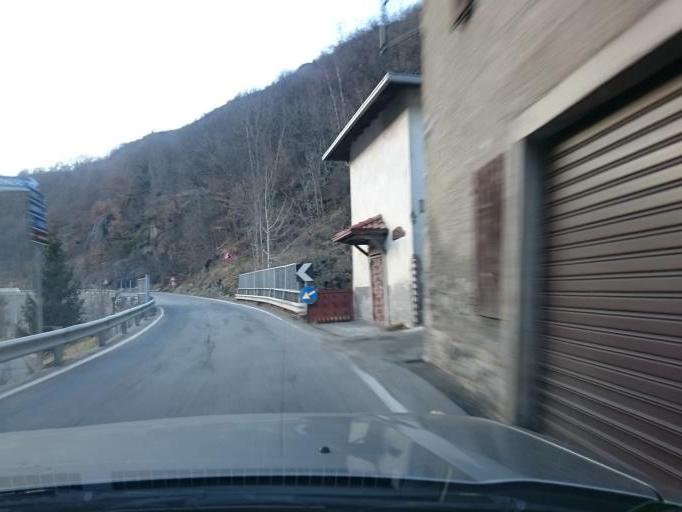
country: IT
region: Lombardy
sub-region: Provincia di Brescia
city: Corteno Golgi
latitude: 46.1693
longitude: 10.2477
